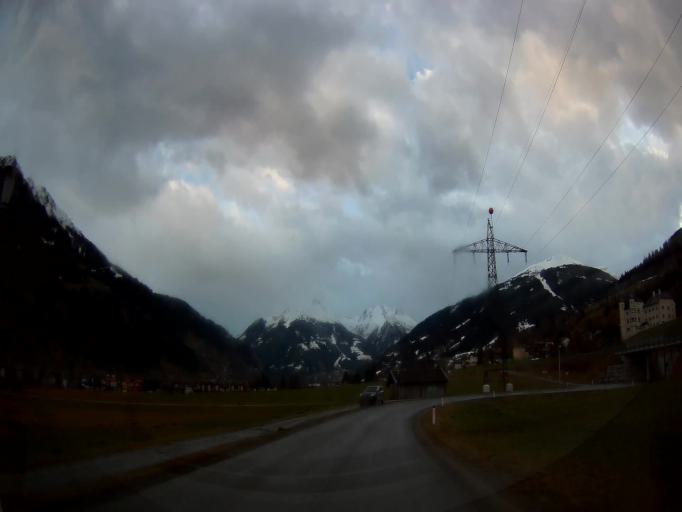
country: AT
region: Salzburg
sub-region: Politischer Bezirk Sankt Johann im Pongau
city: Bad Hofgastein
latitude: 47.1645
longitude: 13.1002
